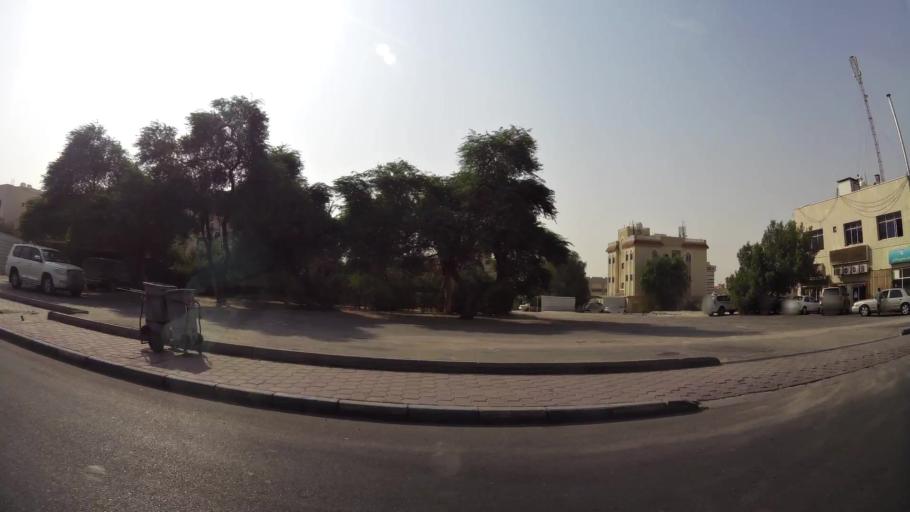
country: KW
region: Al Asimah
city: Ar Rabiyah
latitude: 29.2745
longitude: 47.8716
